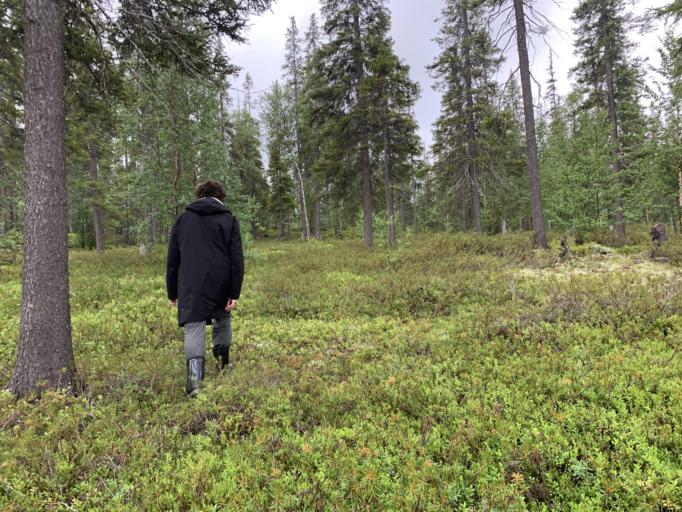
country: RU
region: Murmansk
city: Afrikanda
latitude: 67.6605
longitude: 32.9131
